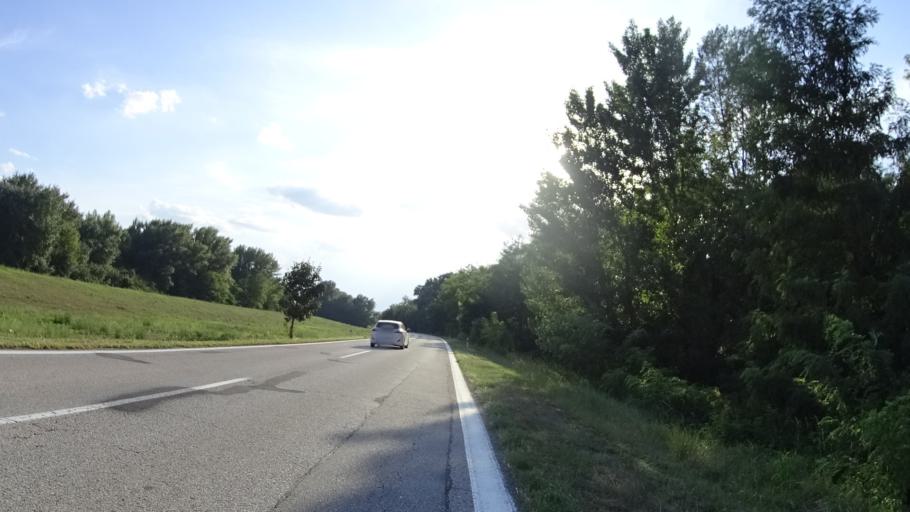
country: HU
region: Komarom-Esztergom
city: Nyergesujfalu
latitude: 47.7731
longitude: 18.5485
